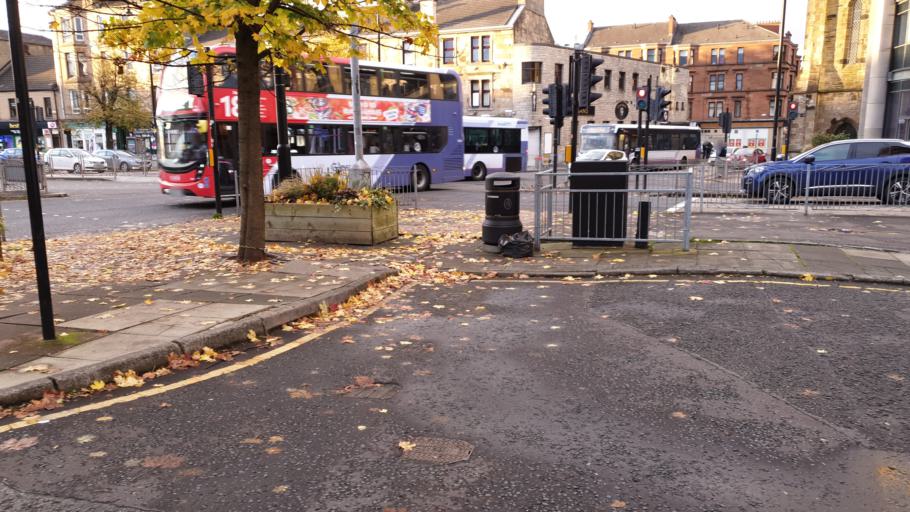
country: GB
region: Scotland
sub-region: South Lanarkshire
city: Rutherglen
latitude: 55.8282
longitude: -4.2102
